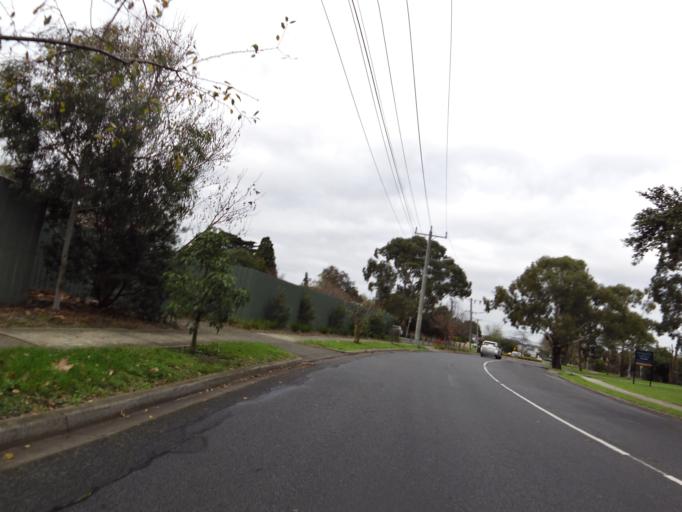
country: AU
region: Victoria
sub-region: Banyule
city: Bellfield
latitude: -37.7551
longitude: 145.0344
